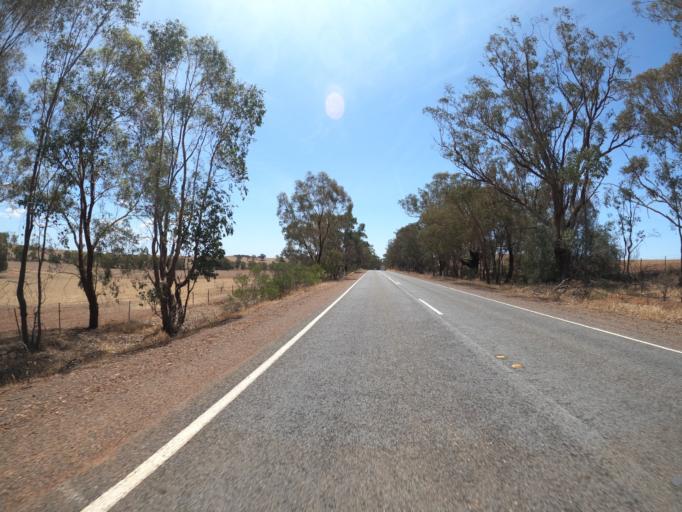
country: AU
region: Victoria
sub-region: Benalla
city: Benalla
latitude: -36.3390
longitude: 145.9590
